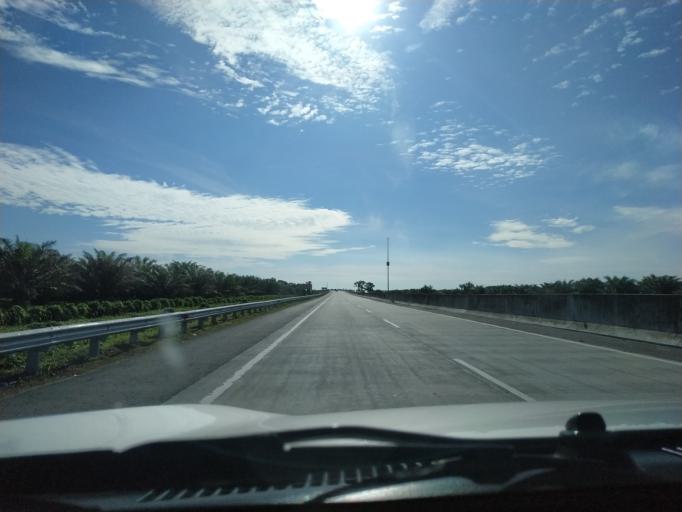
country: ID
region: North Sumatra
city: Percut
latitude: 3.5333
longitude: 98.8698
